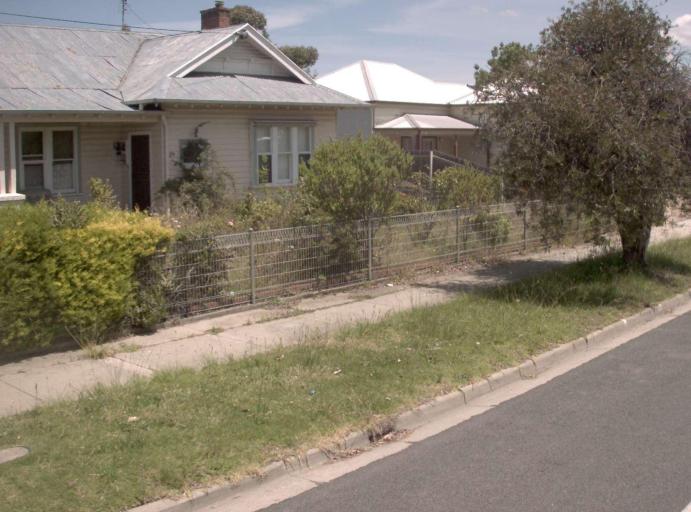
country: AU
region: Victoria
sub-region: East Gippsland
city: Bairnsdale
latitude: -37.8289
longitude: 147.6188
